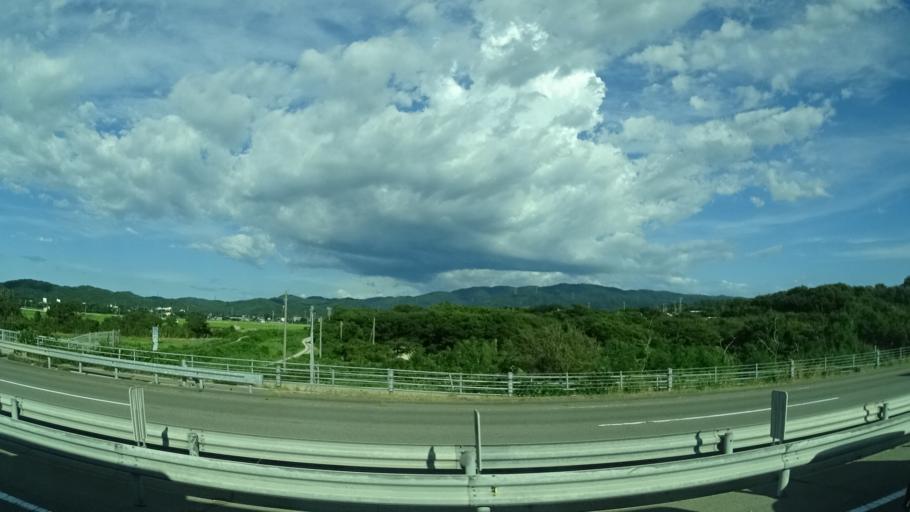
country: JP
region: Ishikawa
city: Hakui
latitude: 36.8230
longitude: 136.7431
